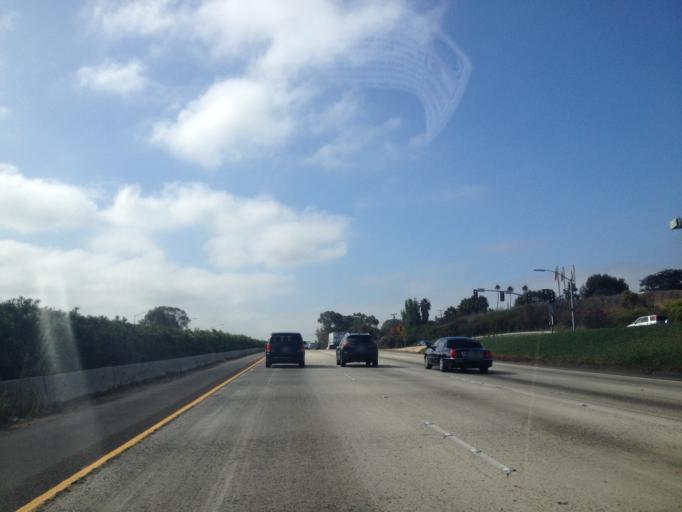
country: US
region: California
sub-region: San Diego County
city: Encinitas
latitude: 33.0649
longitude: -117.2923
